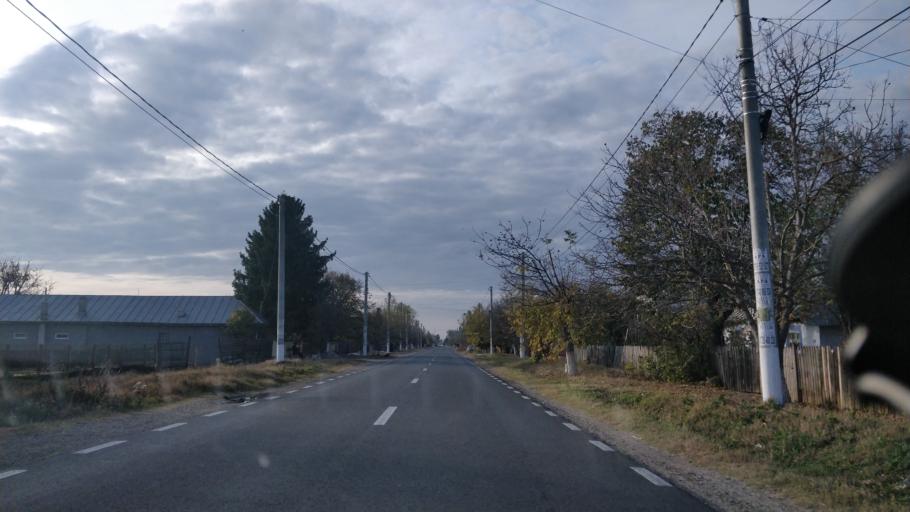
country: RO
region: Giurgiu
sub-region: Comuna Clejani
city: Clejani
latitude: 44.3401
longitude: 25.6833
